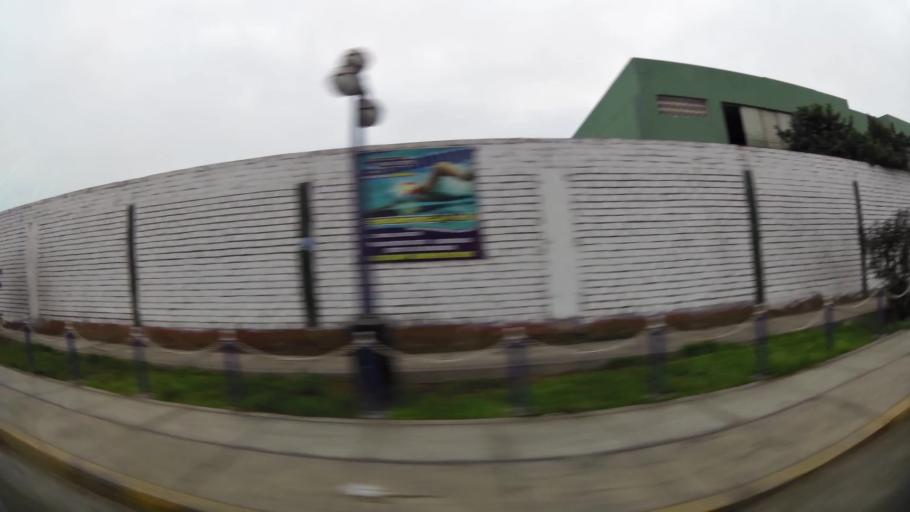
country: PE
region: Lima
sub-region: Lima
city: Surco
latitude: -12.1638
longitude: -77.0195
